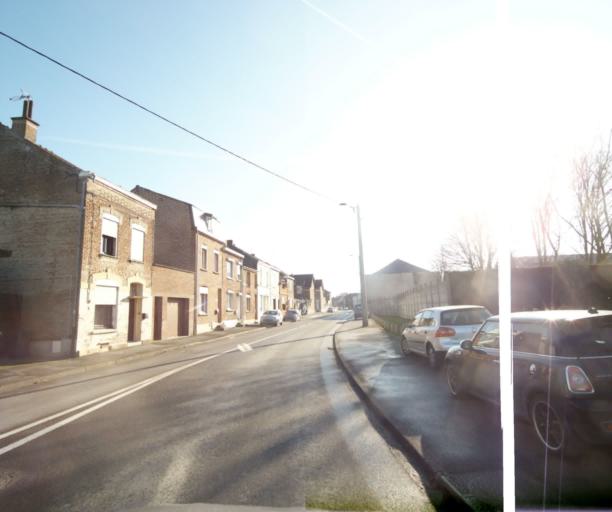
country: FR
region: Nord-Pas-de-Calais
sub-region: Departement du Nord
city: Marly
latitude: 50.3474
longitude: 3.5429
